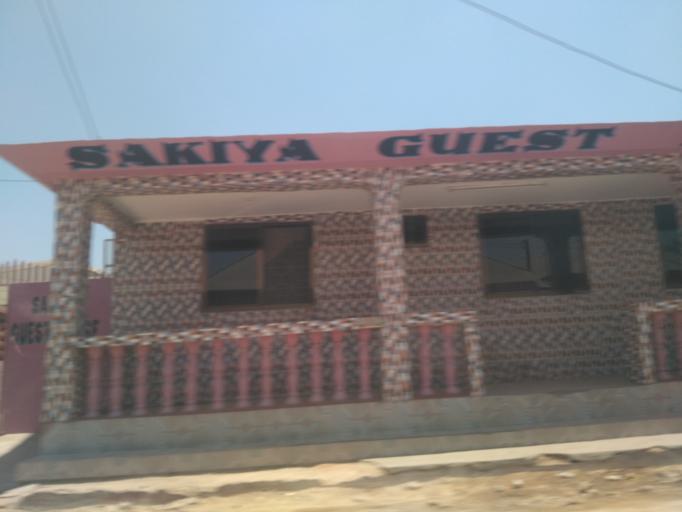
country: TZ
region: Dodoma
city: Dodoma
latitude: -6.1763
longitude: 35.7424
